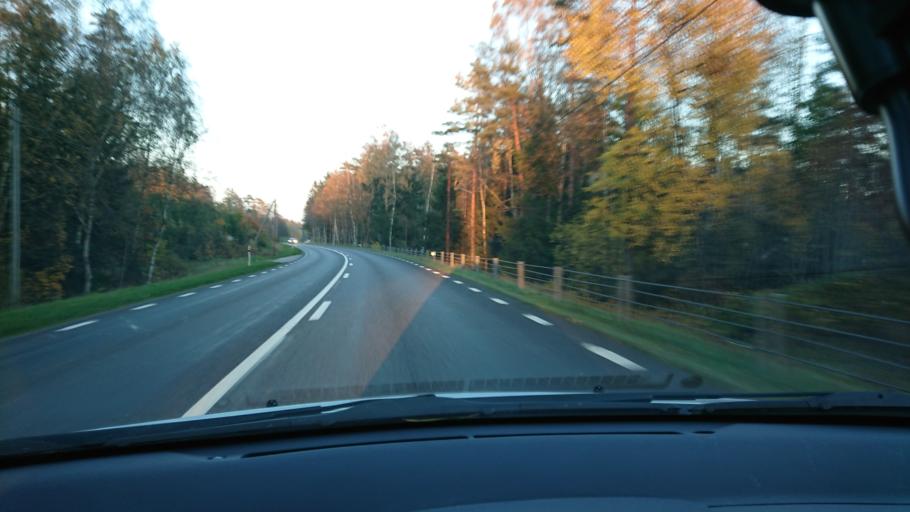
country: SE
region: Halland
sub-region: Halmstads Kommun
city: Oskarstrom
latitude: 56.7135
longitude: 13.1025
